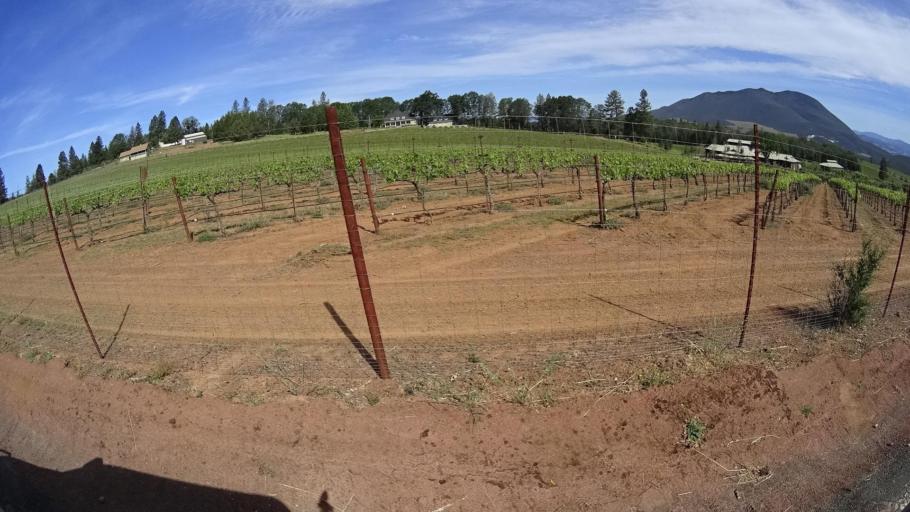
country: US
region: California
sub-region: Lake County
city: Soda Bay
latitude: 38.9137
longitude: -122.7561
